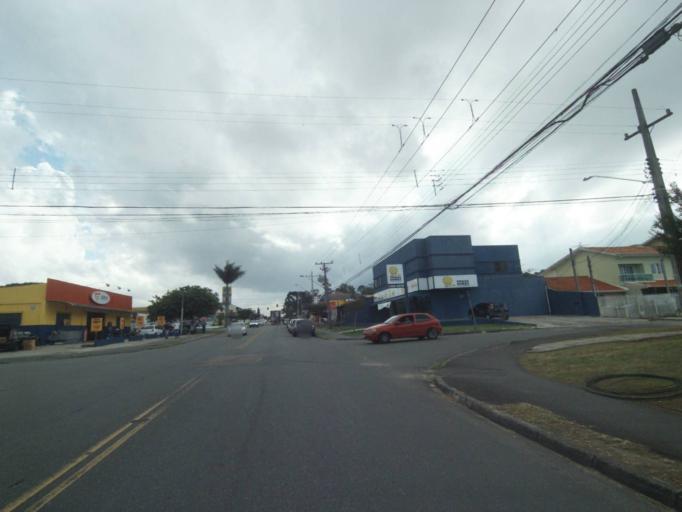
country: BR
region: Parana
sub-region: Pinhais
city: Pinhais
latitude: -25.4509
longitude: -49.2089
